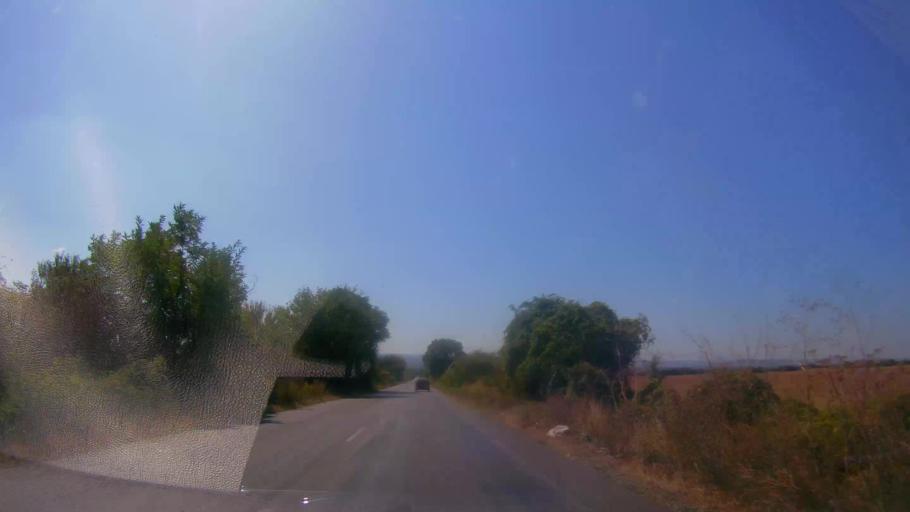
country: BG
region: Veliko Turnovo
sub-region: Obshtina Gorna Oryakhovitsa
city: Purvomaytsi
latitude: 43.2280
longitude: 25.6391
